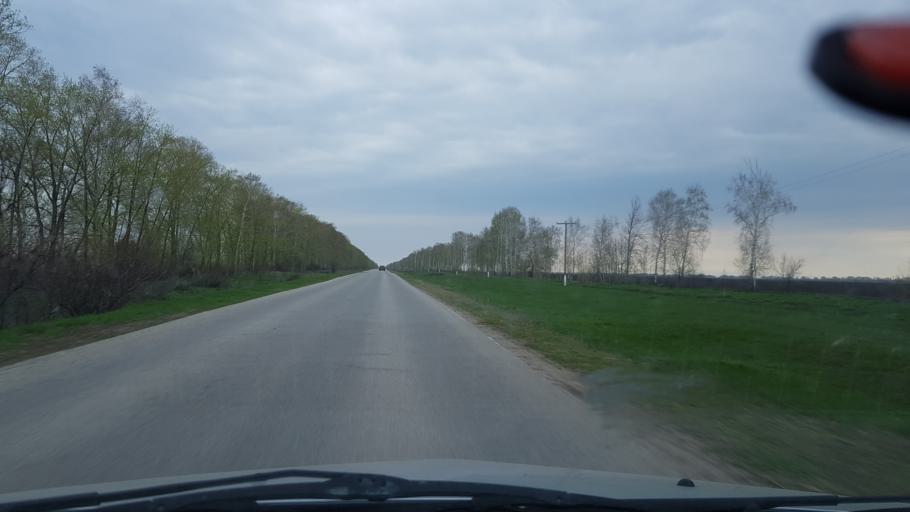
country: RU
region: Samara
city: Tol'yatti
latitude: 53.6587
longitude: 49.2373
